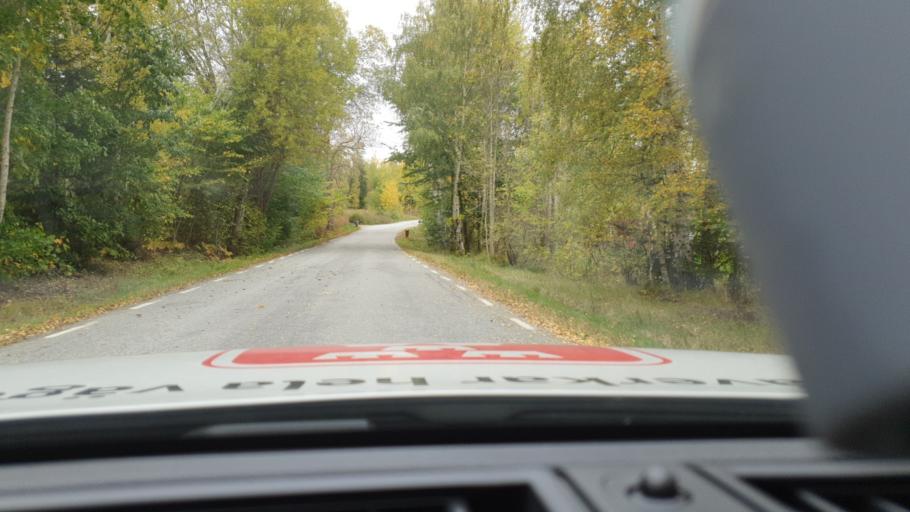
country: SE
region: Stockholm
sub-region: Upplands-Bro Kommun
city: Bro
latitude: 59.4891
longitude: 17.5673
